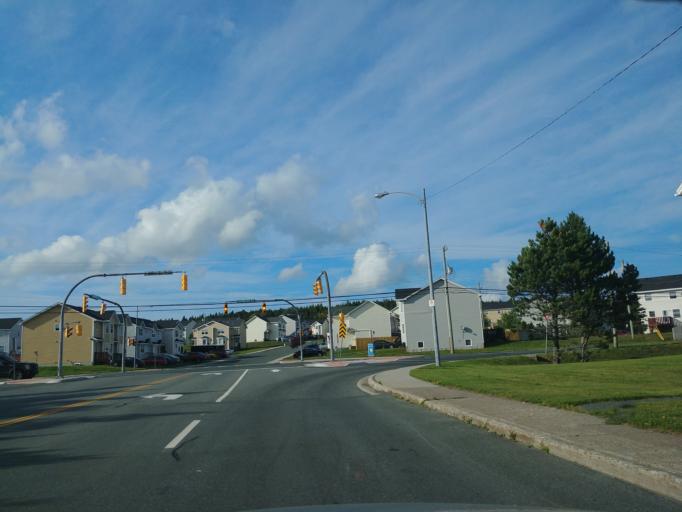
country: CA
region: Newfoundland and Labrador
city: Mount Pearl
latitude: 47.5641
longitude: -52.7654
